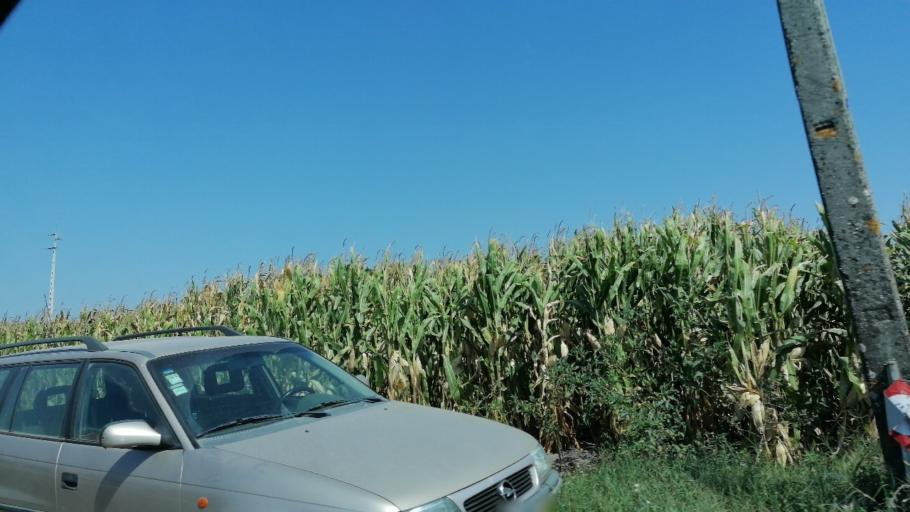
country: PT
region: Santarem
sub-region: Benavente
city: Poceirao
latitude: 38.7008
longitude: -8.7233
